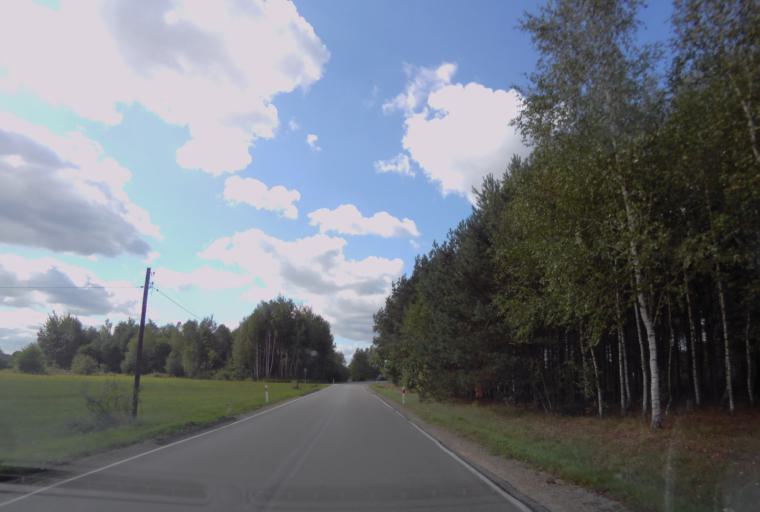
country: PL
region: Subcarpathian Voivodeship
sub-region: Powiat tarnobrzeski
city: Nowa Deba
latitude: 50.4085
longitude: 21.8217
